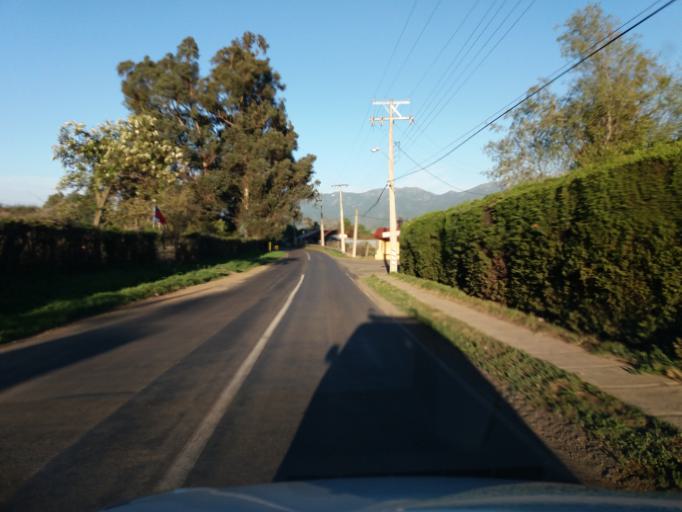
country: CL
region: Valparaiso
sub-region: Provincia de Quillota
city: Quillota
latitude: -32.8950
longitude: -71.2898
